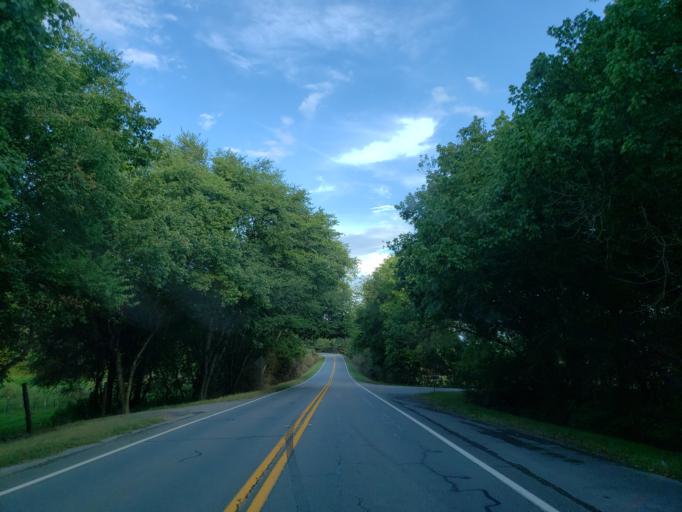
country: US
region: Georgia
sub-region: Bartow County
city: Euharlee
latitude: 34.2427
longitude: -84.8893
